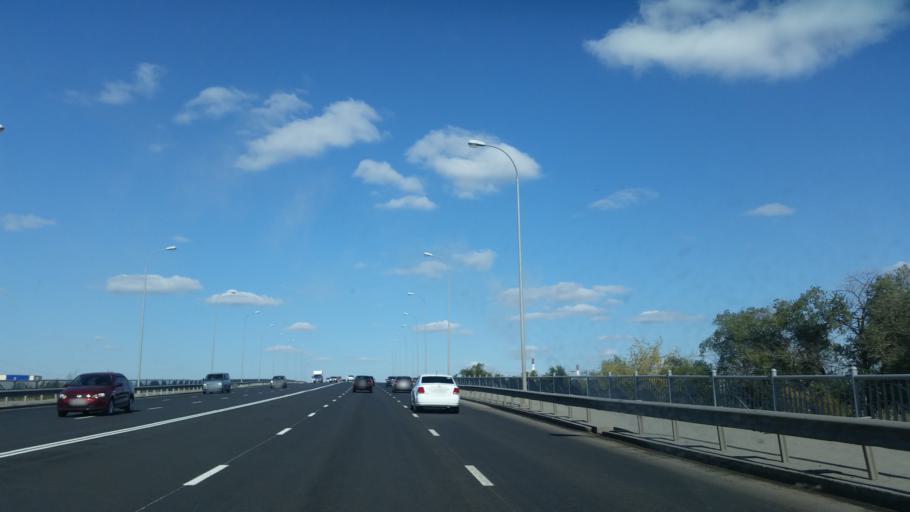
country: KZ
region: Astana Qalasy
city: Astana
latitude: 51.1692
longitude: 71.4792
